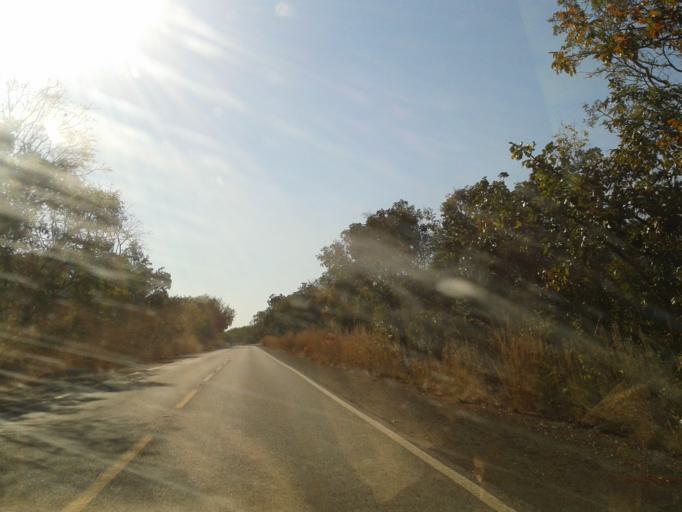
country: BR
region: Goias
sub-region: Mozarlandia
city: Mozarlandia
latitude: -14.9342
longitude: -50.5638
